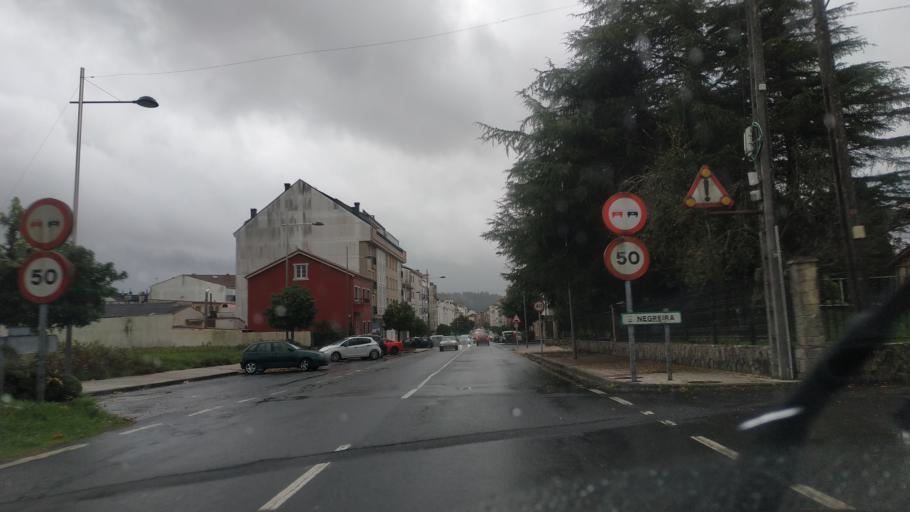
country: ES
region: Galicia
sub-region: Provincia da Coruna
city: Negreira
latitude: 42.9167
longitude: -8.7347
